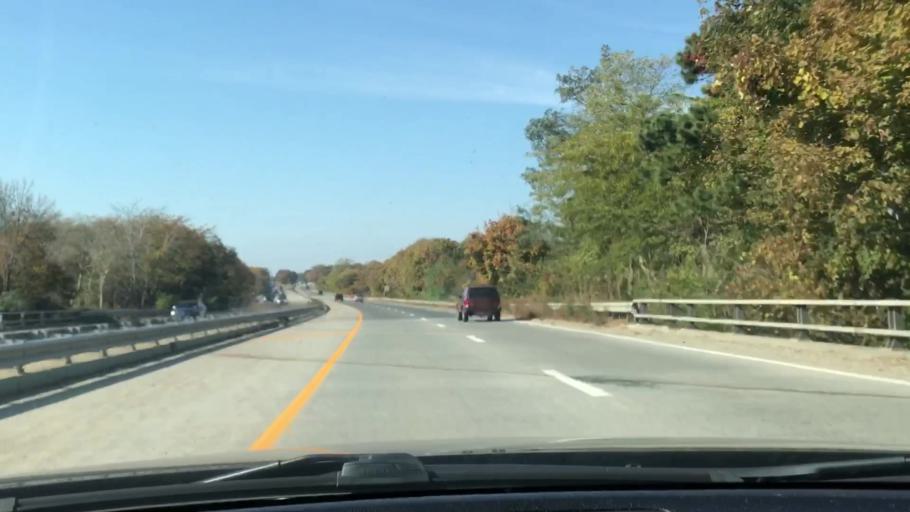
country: US
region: New York
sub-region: Suffolk County
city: Hampton Bays
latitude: 40.8907
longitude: -72.4980
